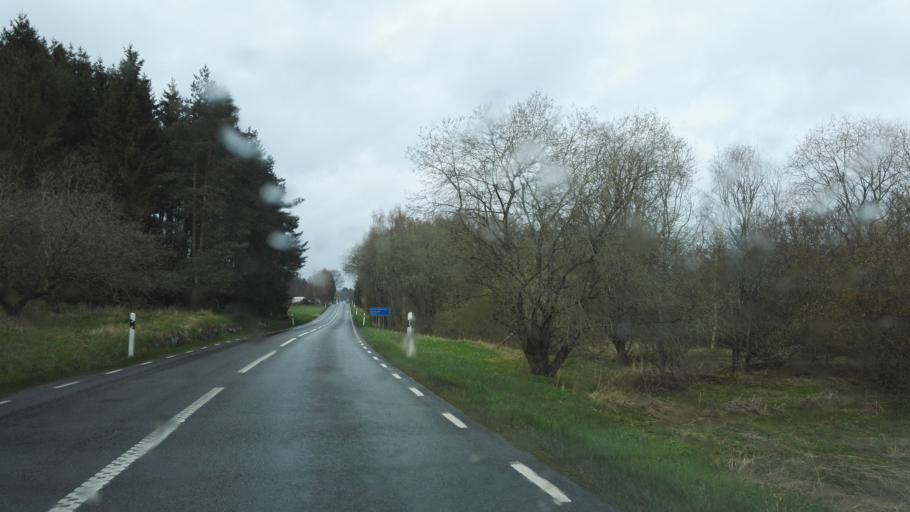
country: SE
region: Skane
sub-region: Simrishamns Kommun
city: Kivik
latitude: 55.6657
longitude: 14.2224
